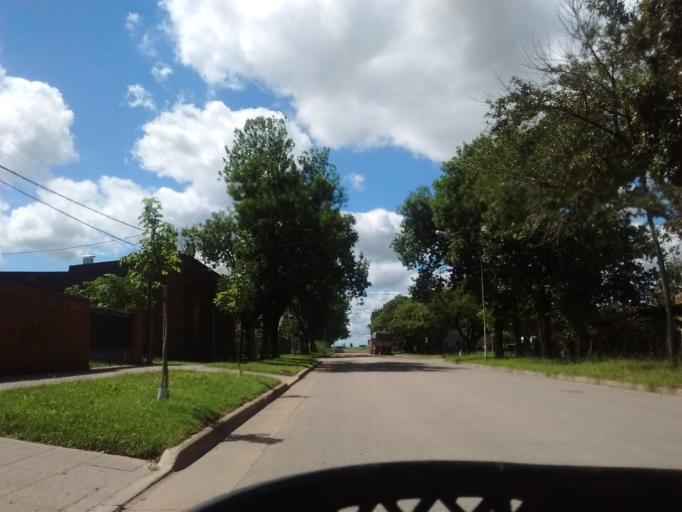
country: AR
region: Santa Fe
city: Galvez
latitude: -31.9053
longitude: -61.2763
